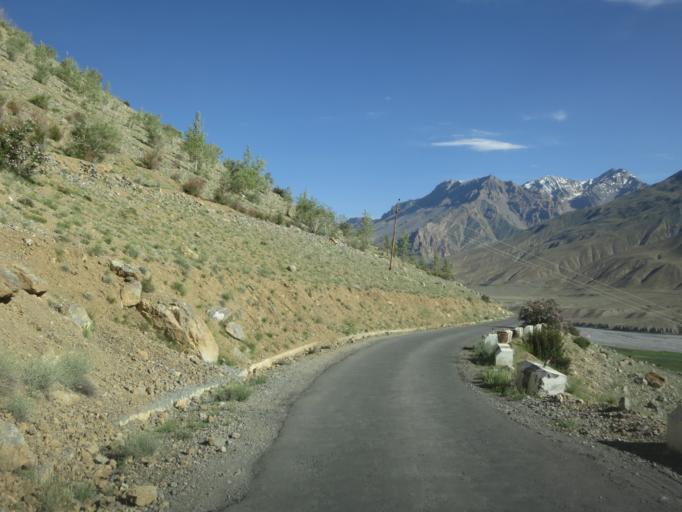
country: IN
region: Himachal Pradesh
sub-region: Shimla
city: Sarahan
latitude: 32.2984
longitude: 78.0096
